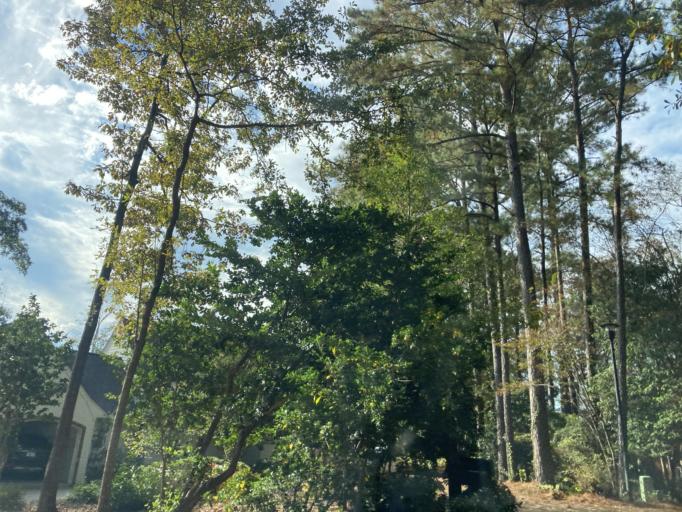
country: US
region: Mississippi
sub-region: Lamar County
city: West Hattiesburg
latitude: 31.3268
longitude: -89.4581
